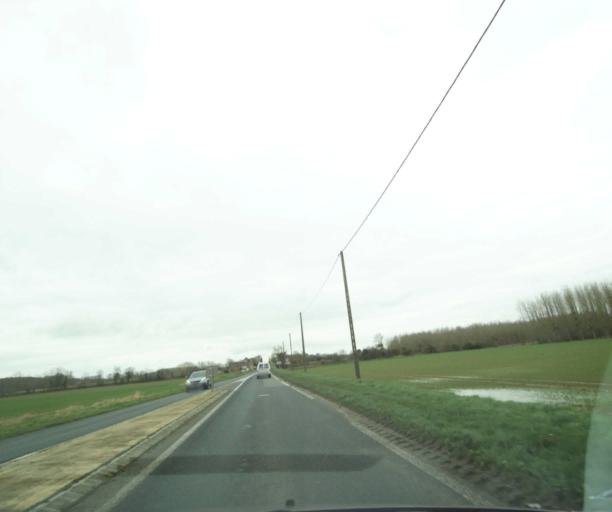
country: FR
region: Picardie
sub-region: Departement de l'Oise
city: Noyon
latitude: 49.5906
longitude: 2.9853
